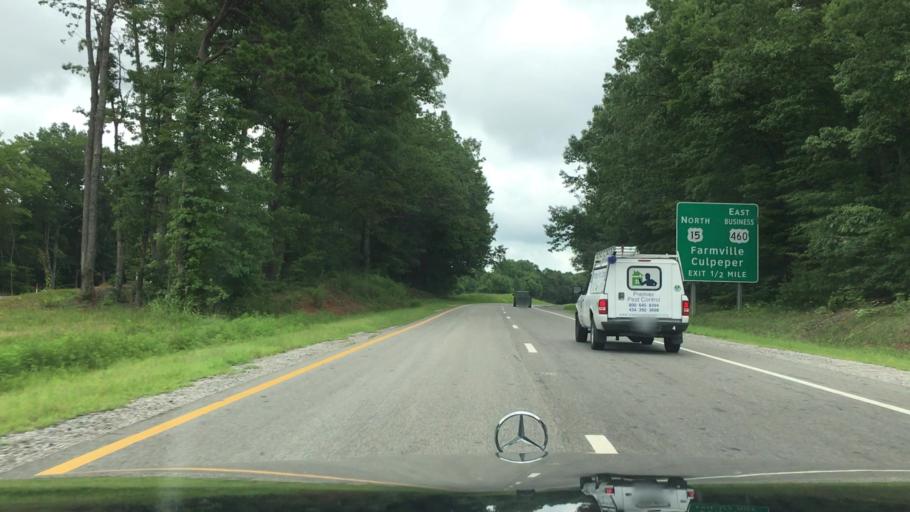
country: US
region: Virginia
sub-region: Prince Edward County
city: Hampden Sydney
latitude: 37.3156
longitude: -78.4744
